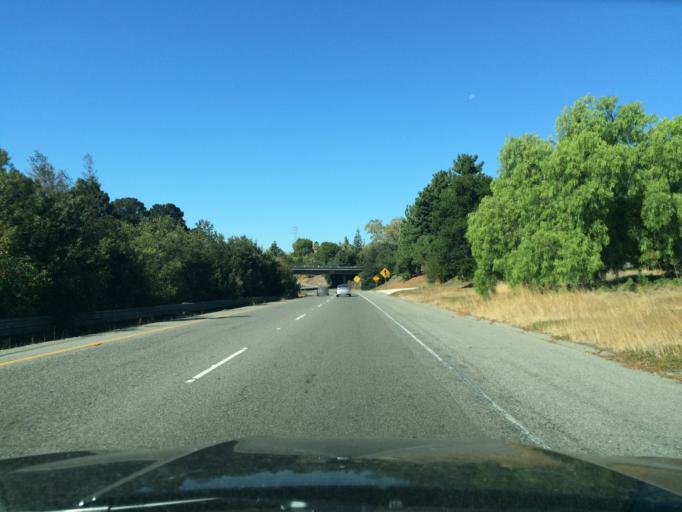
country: US
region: California
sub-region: Santa Clara County
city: Mountain View
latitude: 37.3860
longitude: -122.0624
